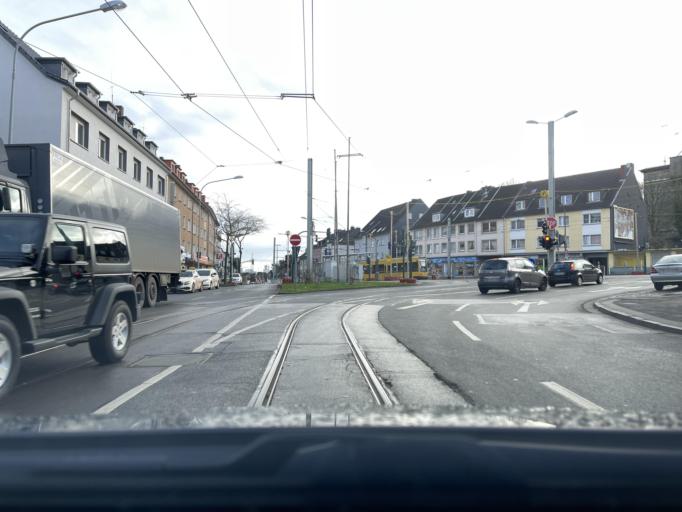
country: DE
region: North Rhine-Westphalia
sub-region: Regierungsbezirk Munster
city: Bottrop
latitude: 51.4641
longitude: 6.9475
